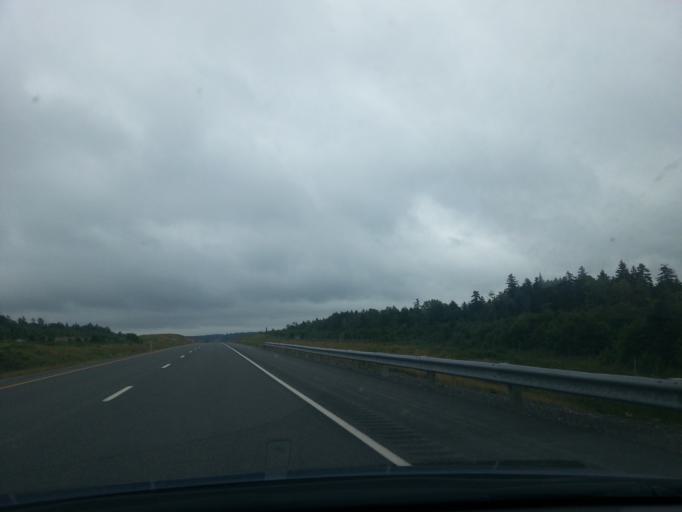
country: CA
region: New Brunswick
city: Nackawic
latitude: 45.9152
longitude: -67.1303
